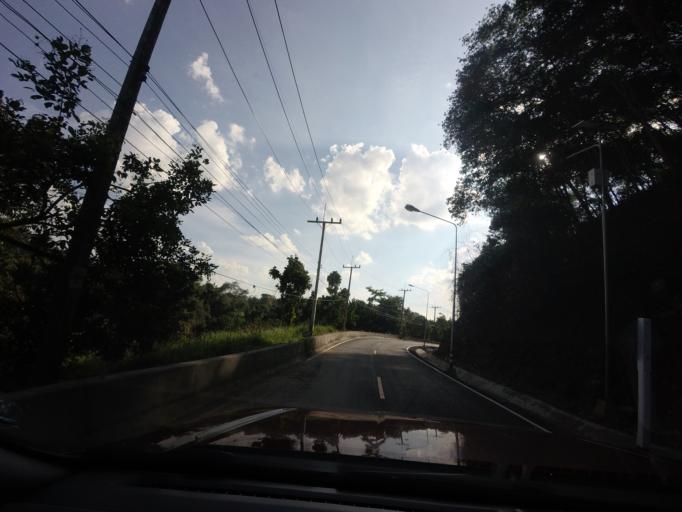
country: TH
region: Yala
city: Than To
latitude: 6.1280
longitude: 101.2990
